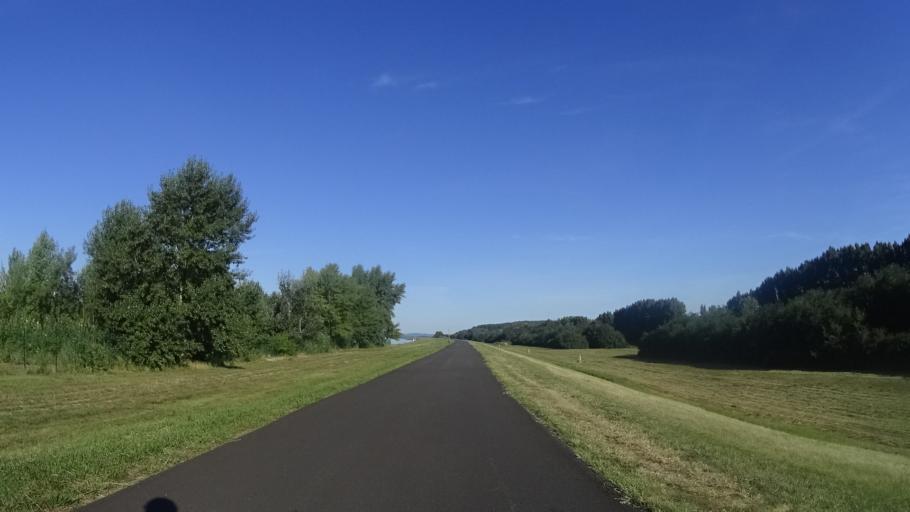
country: SK
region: Trnavsky
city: Samorin
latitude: 48.0208
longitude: 17.2797
